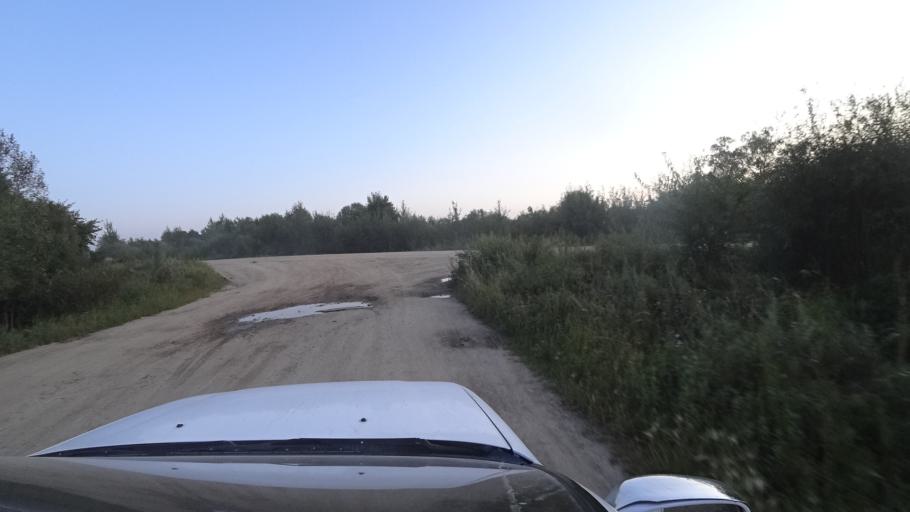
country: RU
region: Primorskiy
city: Dal'nerechensk
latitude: 45.9433
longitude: 133.7601
